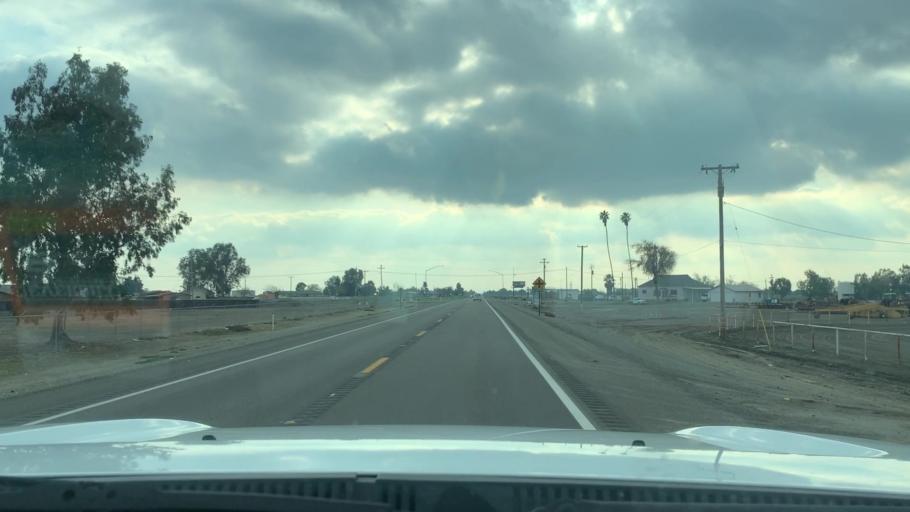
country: US
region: California
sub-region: Kings County
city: Stratford
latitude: 36.1913
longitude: -119.8266
